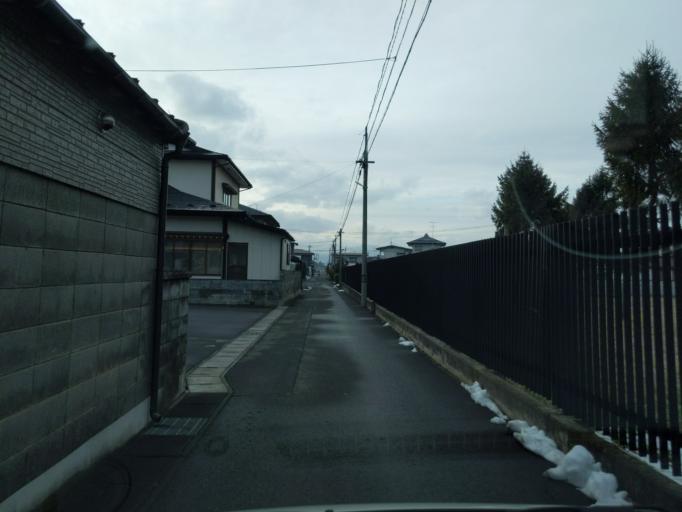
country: JP
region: Iwate
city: Mizusawa
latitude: 39.1329
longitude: 141.1320
